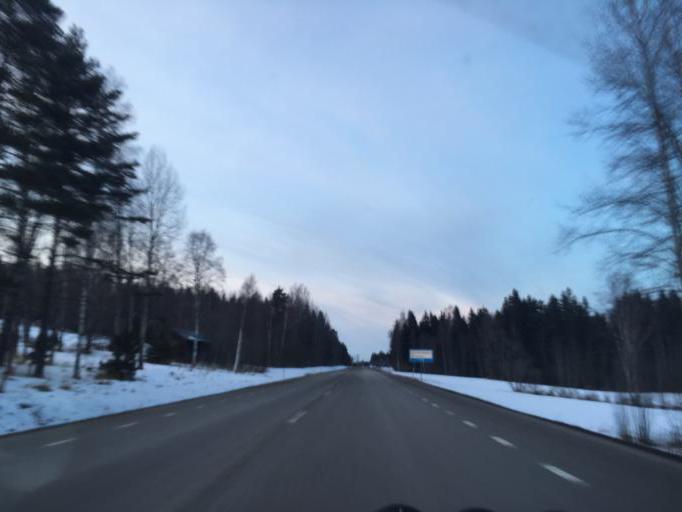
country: SE
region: Dalarna
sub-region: Leksand Municipality
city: Leksand
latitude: 60.8074
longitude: 15.0498
